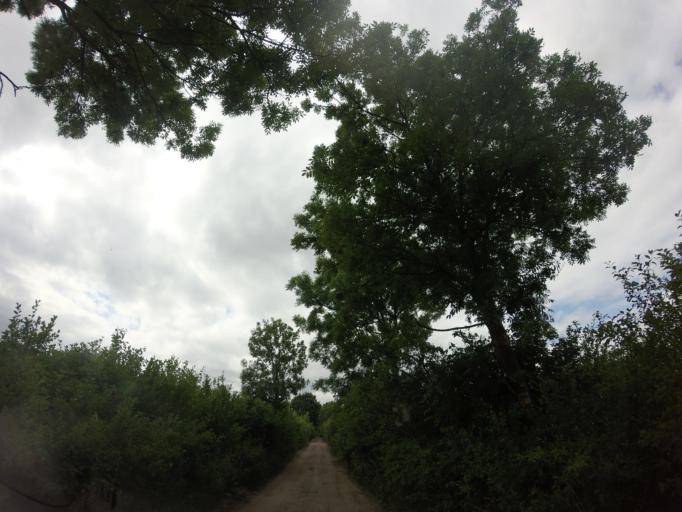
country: PL
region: Lubusz
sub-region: Powiat strzelecko-drezdenecki
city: Strzelce Krajenskie
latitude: 52.9453
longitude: 15.6083
